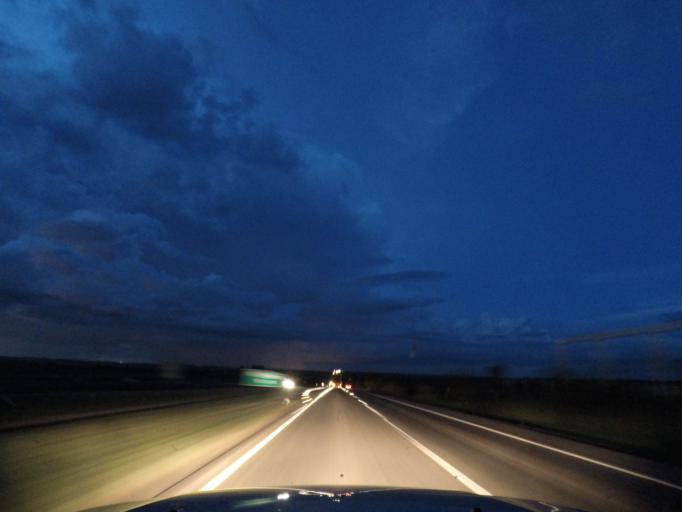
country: BR
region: Minas Gerais
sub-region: Uberlandia
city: Uberlandia
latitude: -19.2238
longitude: -48.1448
